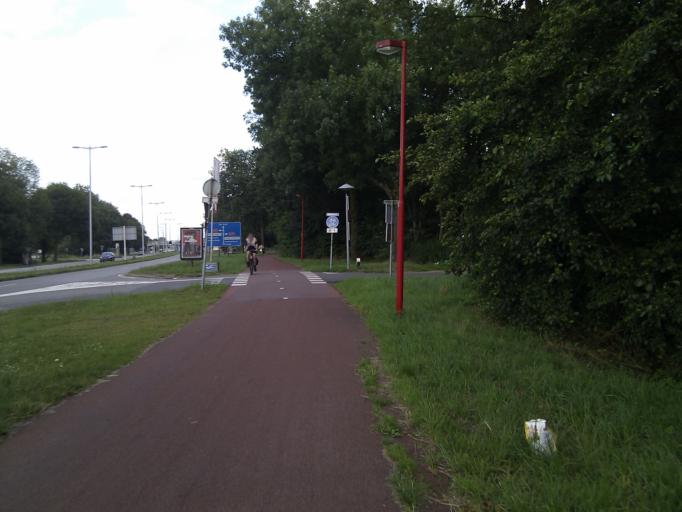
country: NL
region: Utrecht
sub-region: Gemeente Utrecht
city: Utrecht
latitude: 52.1021
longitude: 5.1466
